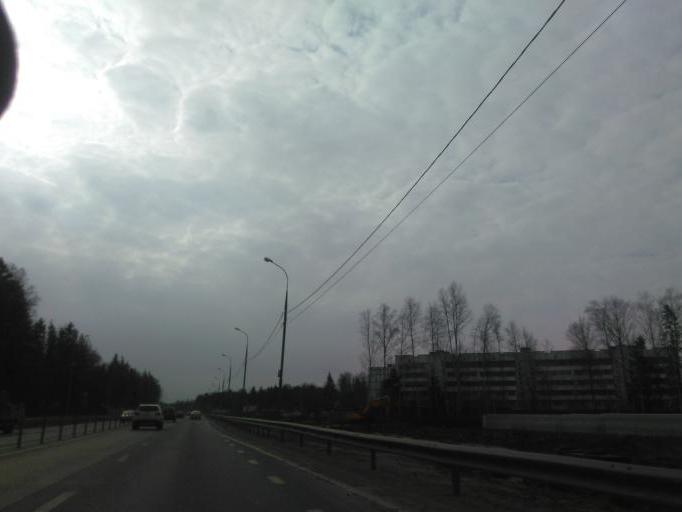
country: RU
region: Moskovskaya
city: Yermolino
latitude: 56.1306
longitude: 37.5083
